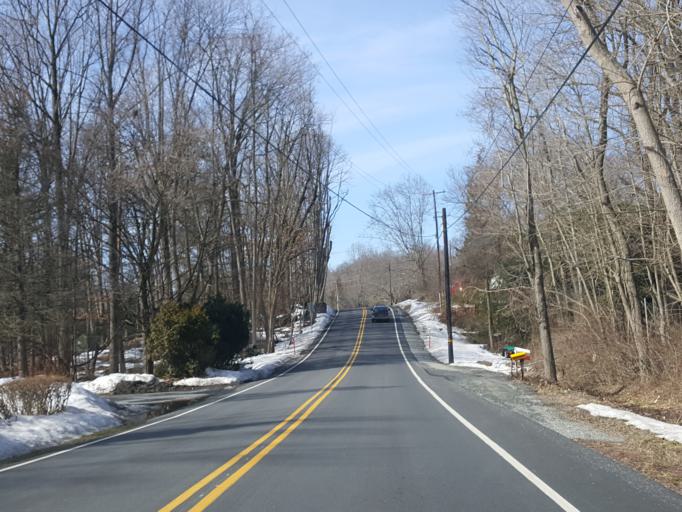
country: US
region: Pennsylvania
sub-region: Lebanon County
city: Campbelltown
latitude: 40.2490
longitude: -76.5405
